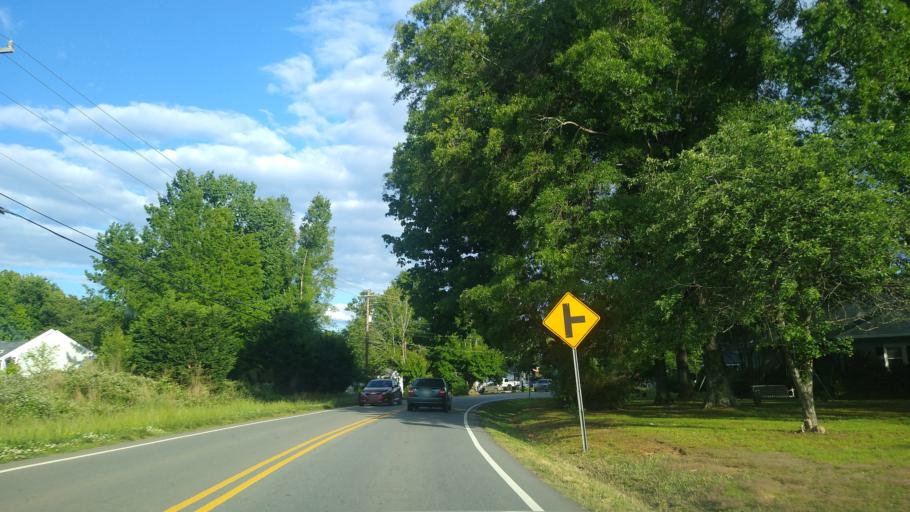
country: US
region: North Carolina
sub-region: Guilford County
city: Greensboro
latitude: 36.1462
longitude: -79.7462
